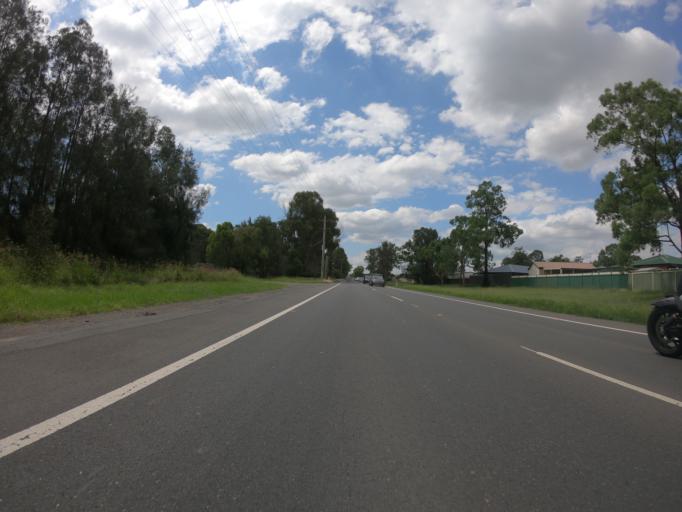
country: AU
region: New South Wales
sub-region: Blacktown
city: Mount Druitt
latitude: -33.7962
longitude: 150.7690
